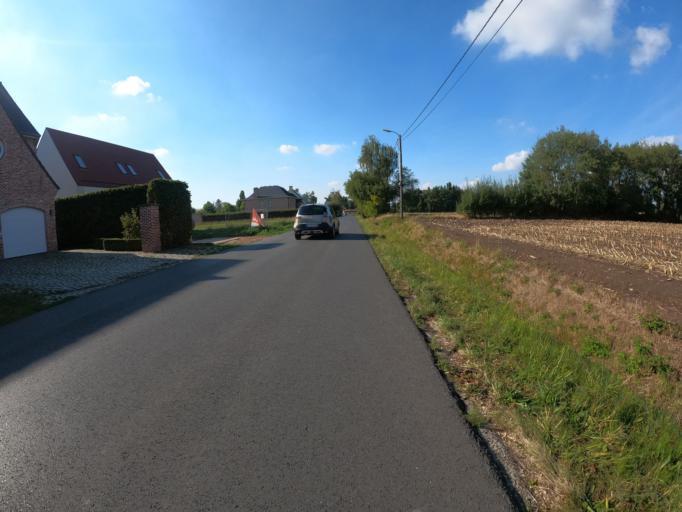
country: BE
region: Flanders
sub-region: Provincie Antwerpen
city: Berlaar
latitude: 51.0784
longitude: 4.6638
